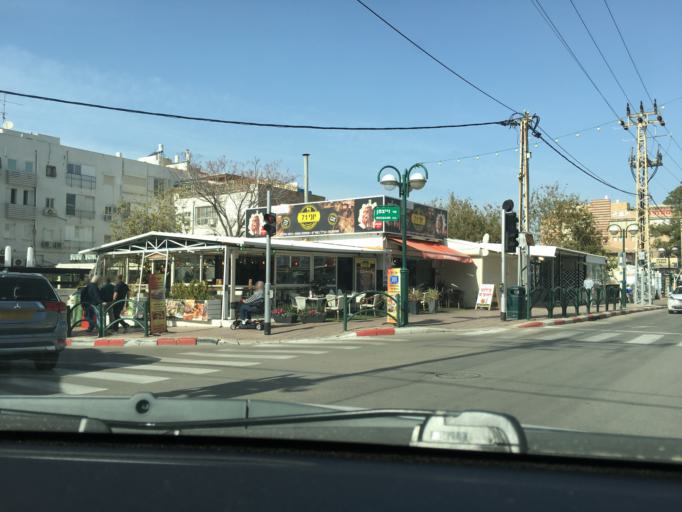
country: IL
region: Tel Aviv
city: Ramat HaSharon
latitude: 32.1460
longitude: 34.8386
